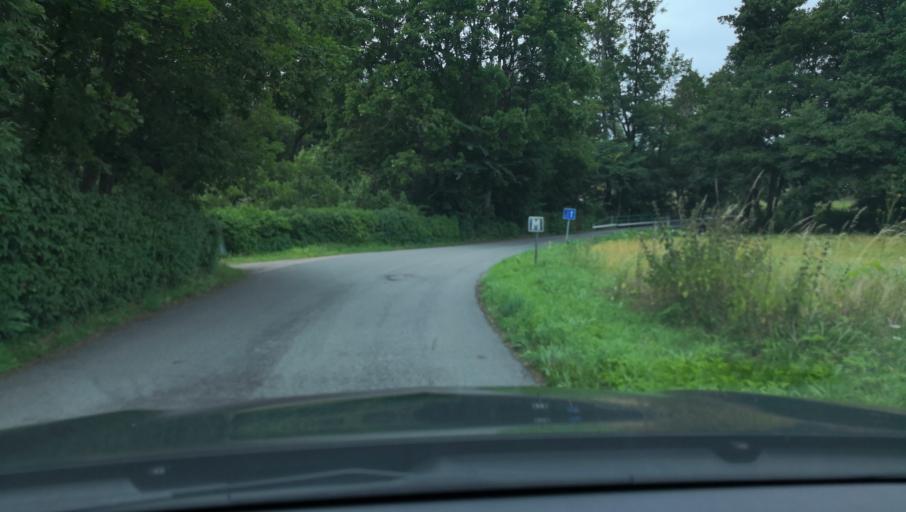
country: SE
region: Skane
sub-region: Simrishamns Kommun
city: Kivik
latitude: 55.7201
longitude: 14.1559
